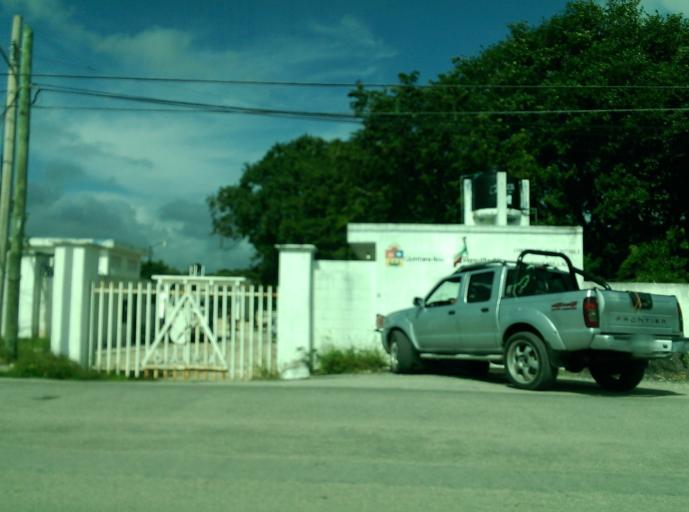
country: MX
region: Quintana Roo
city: Tulum
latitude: 20.2140
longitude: -87.4542
